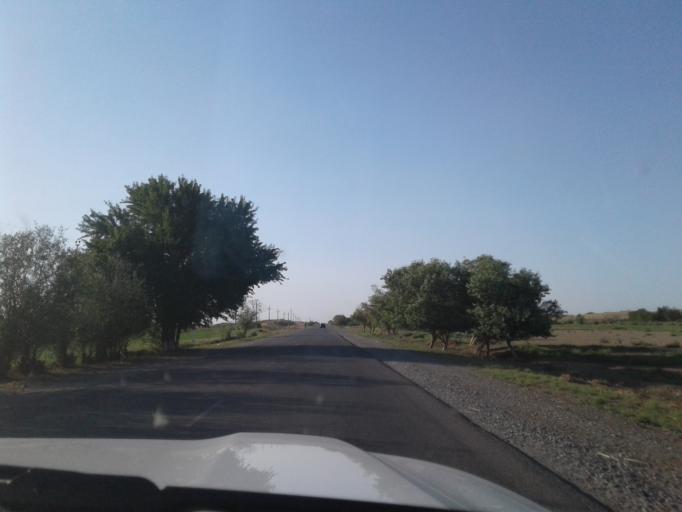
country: TM
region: Mary
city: Yoloeten
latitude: 37.2433
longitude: 62.3689
